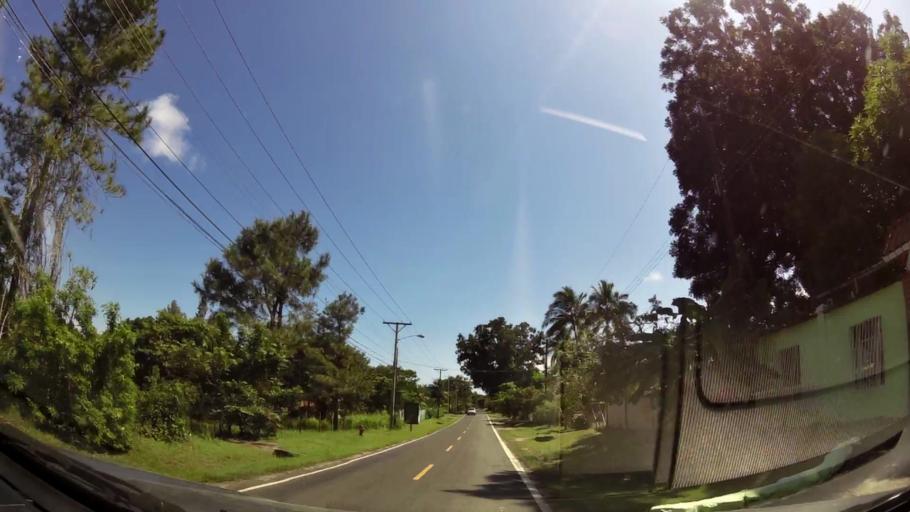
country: PA
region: Panama
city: Chame
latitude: 8.5608
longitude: -79.8883
